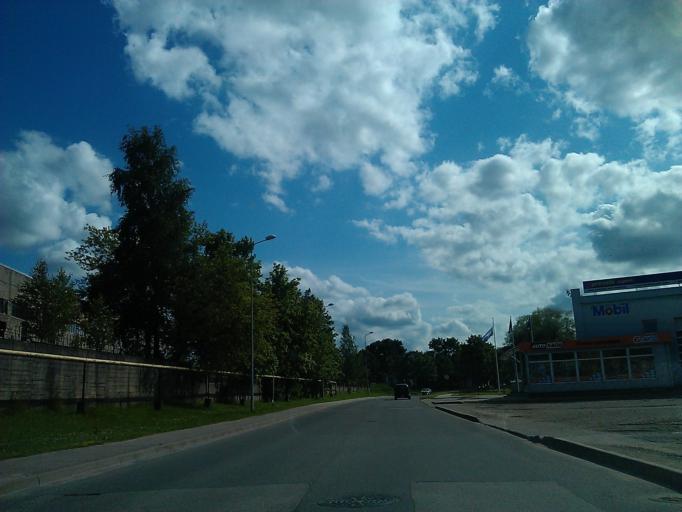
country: LV
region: Cesu Rajons
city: Cesis
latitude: 57.3109
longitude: 25.2860
